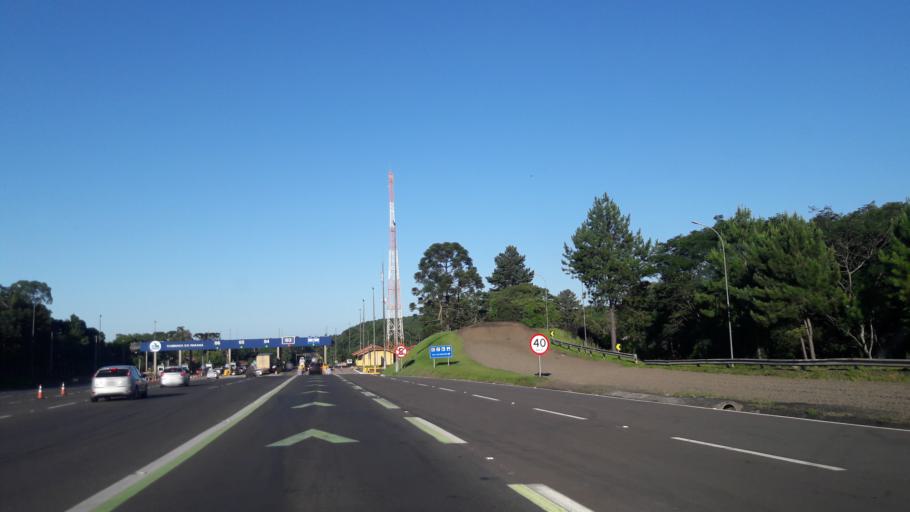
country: BR
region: Parana
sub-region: Prudentopolis
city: Prudentopolis
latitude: -25.3107
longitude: -51.1697
